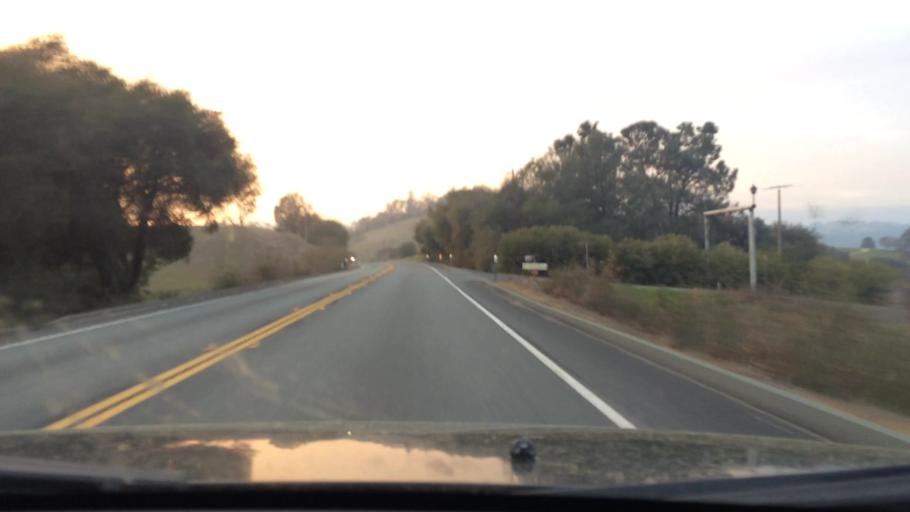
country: US
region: California
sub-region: Amador County
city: Jackson
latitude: 38.2977
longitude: -120.7224
